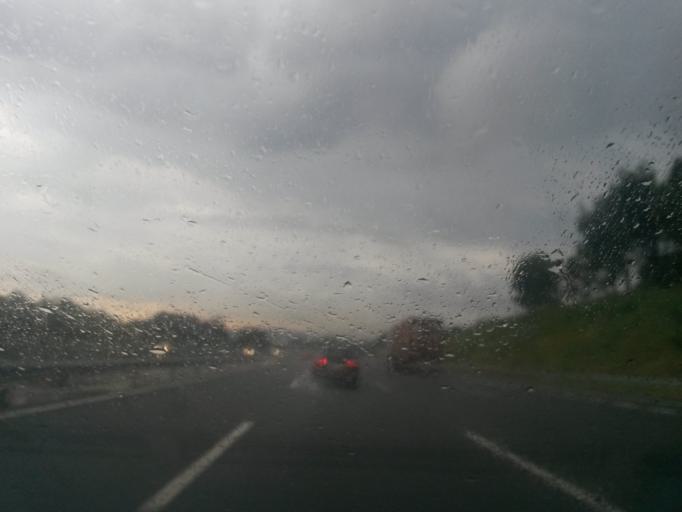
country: ES
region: Catalonia
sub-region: Provincia de Girona
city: Salt
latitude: 41.9932
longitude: 2.7927
